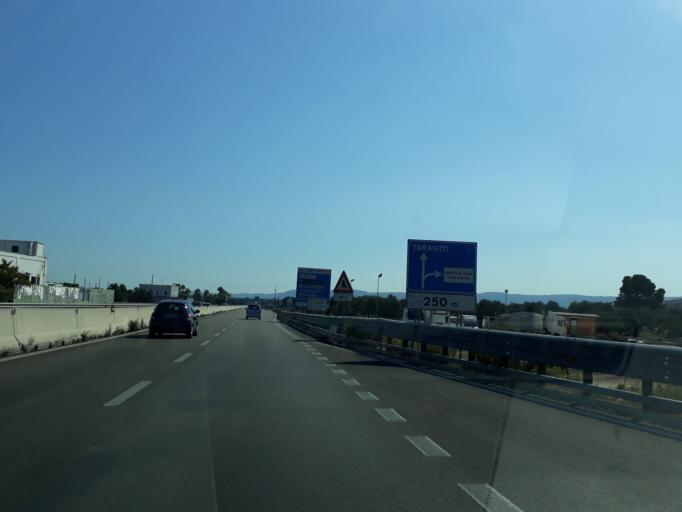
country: IT
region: Apulia
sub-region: Provincia di Brindisi
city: Fasano
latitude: 40.8567
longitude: 17.3512
